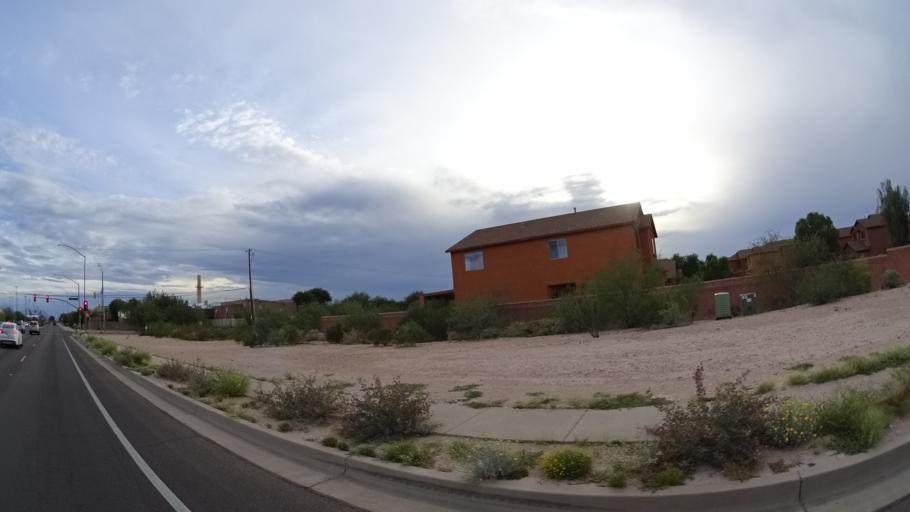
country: US
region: Arizona
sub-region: Pima County
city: South Tucson
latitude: 32.1421
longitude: -110.9349
